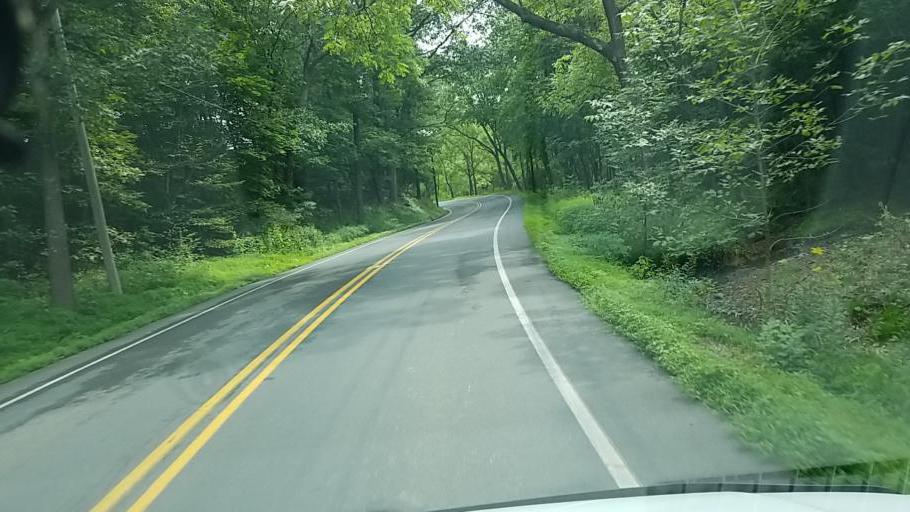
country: US
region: Pennsylvania
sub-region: Dauphin County
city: Elizabethville
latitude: 40.6210
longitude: -76.7850
